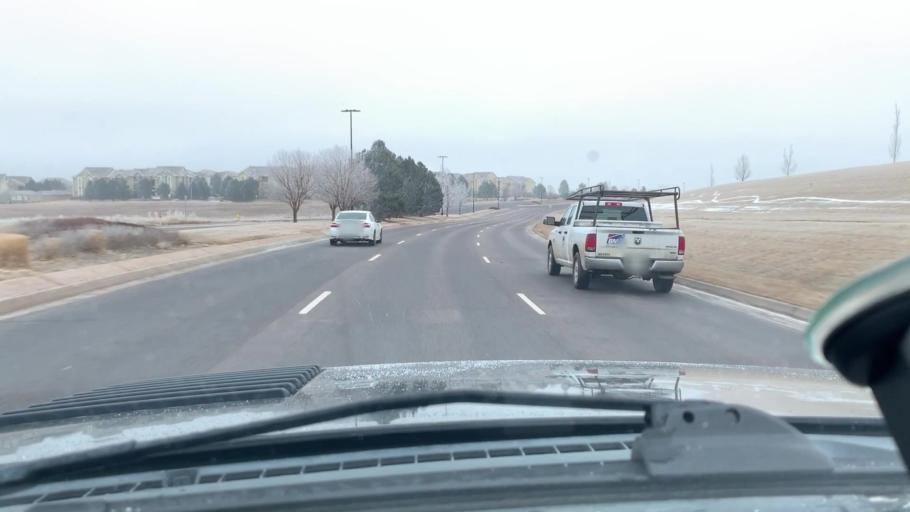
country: US
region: Colorado
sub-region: Arapahoe County
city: Dove Valley
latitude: 39.5781
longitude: -104.8260
